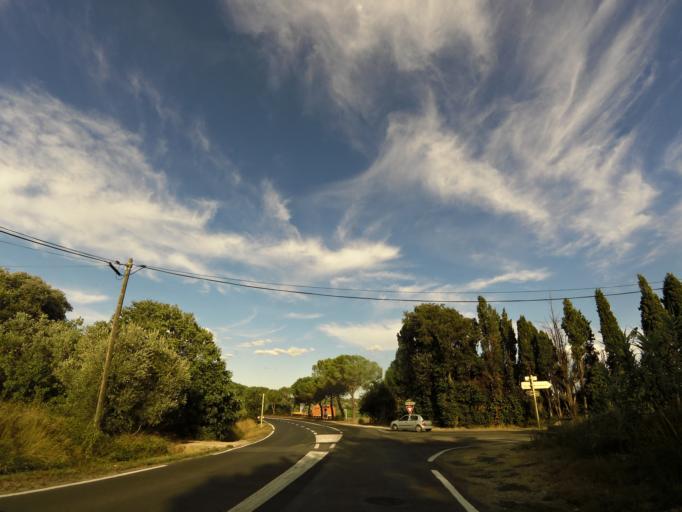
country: FR
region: Languedoc-Roussillon
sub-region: Departement du Gard
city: Sommieres
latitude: 43.7772
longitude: 4.0741
